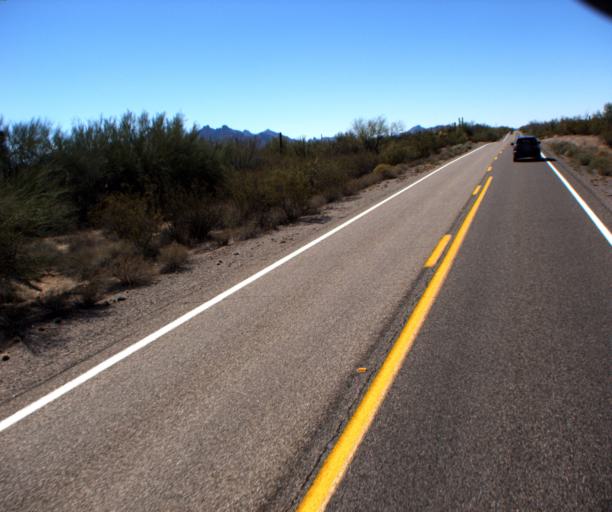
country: US
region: Arizona
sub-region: Pima County
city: Ajo
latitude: 32.1851
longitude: -112.7612
